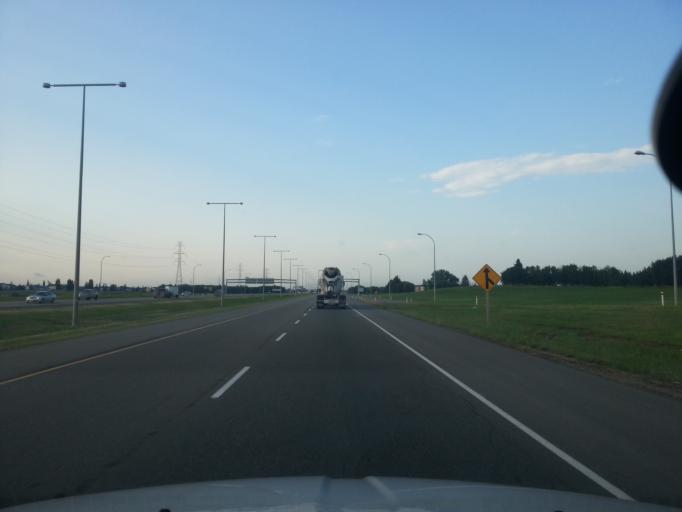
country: CA
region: Alberta
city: St. Albert
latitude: 53.4932
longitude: -113.6597
